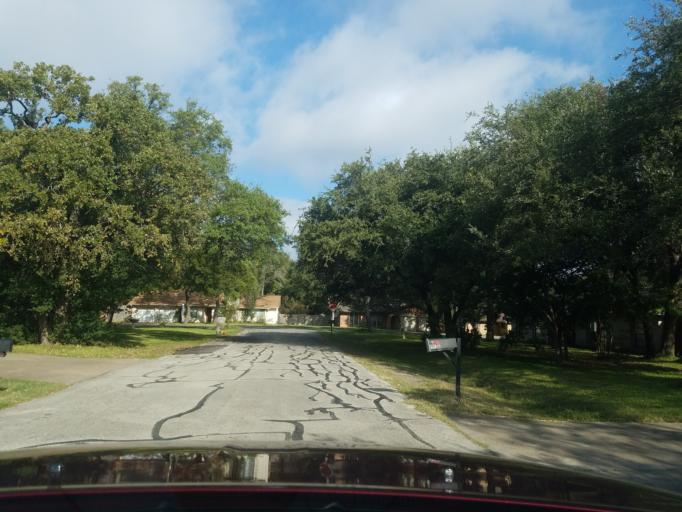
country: US
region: Texas
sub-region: Williamson County
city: Jollyville
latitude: 30.4538
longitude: -97.7819
